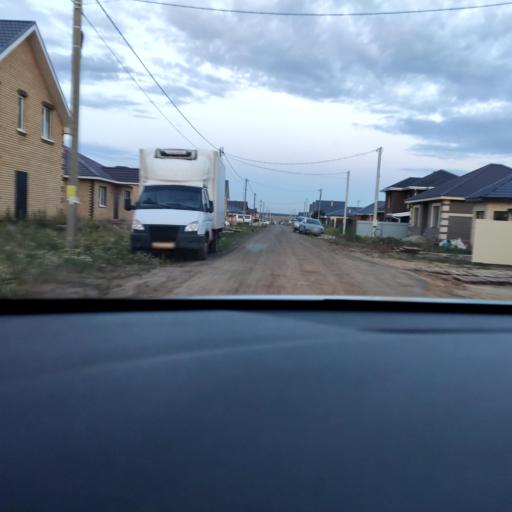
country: RU
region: Tatarstan
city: Stolbishchi
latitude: 55.7170
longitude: 49.2979
